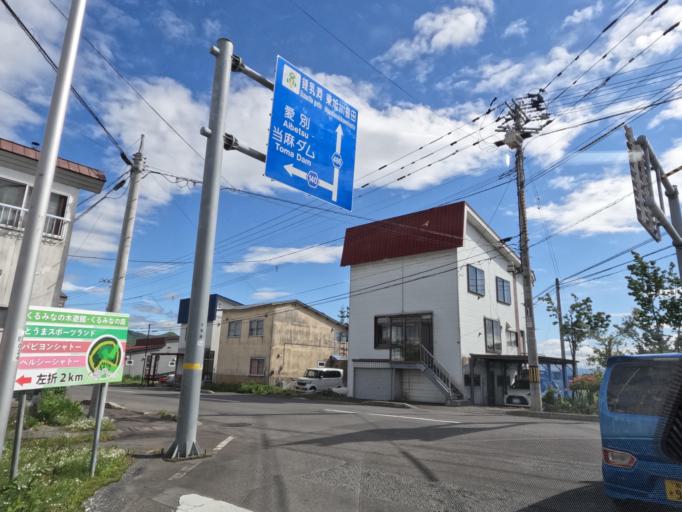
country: JP
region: Hokkaido
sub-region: Asahikawa-shi
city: Asahikawa
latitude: 43.8223
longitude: 142.5169
